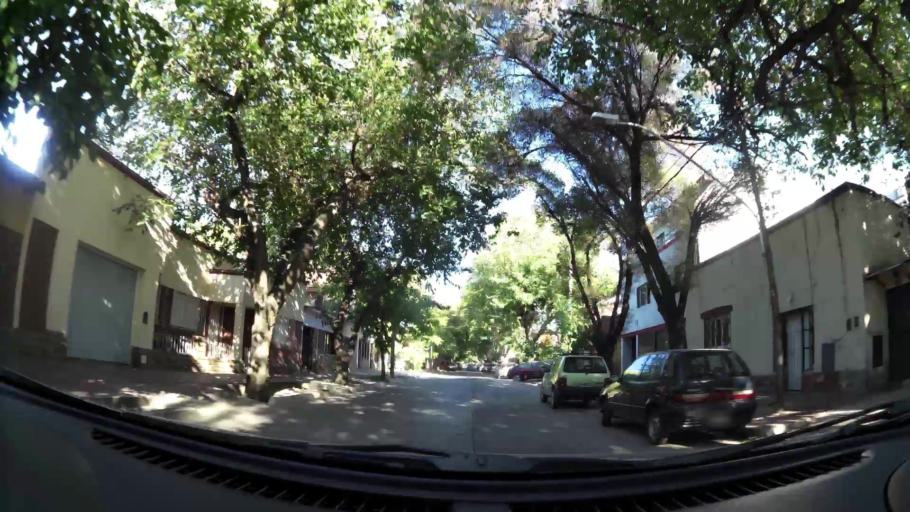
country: AR
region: Mendoza
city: Mendoza
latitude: -32.8743
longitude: -68.8273
